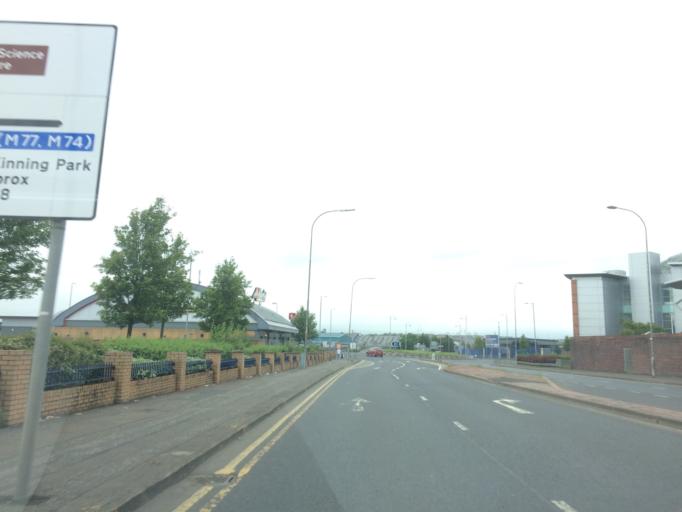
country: GB
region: Scotland
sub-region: East Renfrewshire
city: Giffnock
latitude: 55.8527
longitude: -4.3187
